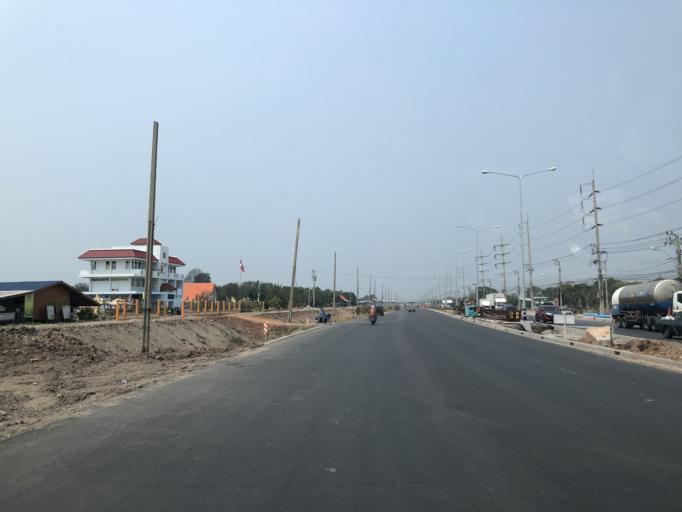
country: TH
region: Samut Prakan
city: Bang Bo
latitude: 13.5096
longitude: 100.8063
